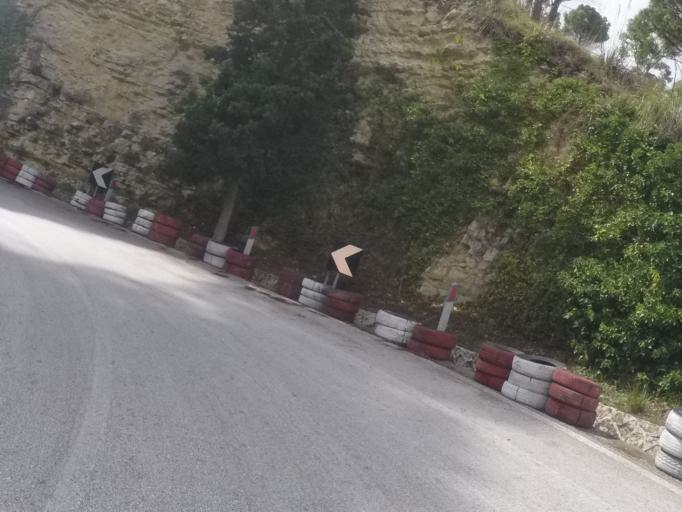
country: IT
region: Sicily
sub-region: Trapani
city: Erice
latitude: 38.0459
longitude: 12.5912
